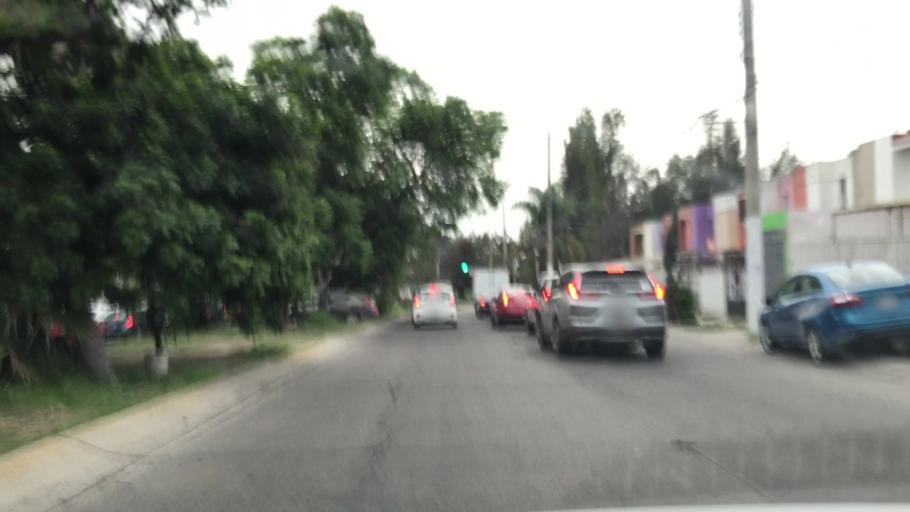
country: MX
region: Jalisco
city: Zapopan2
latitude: 20.7401
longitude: -103.4062
